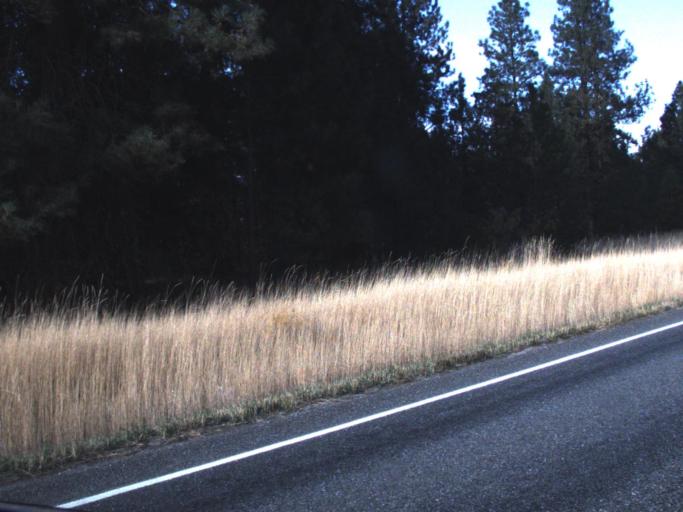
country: US
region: Washington
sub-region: Stevens County
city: Kettle Falls
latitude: 48.5050
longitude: -118.1533
